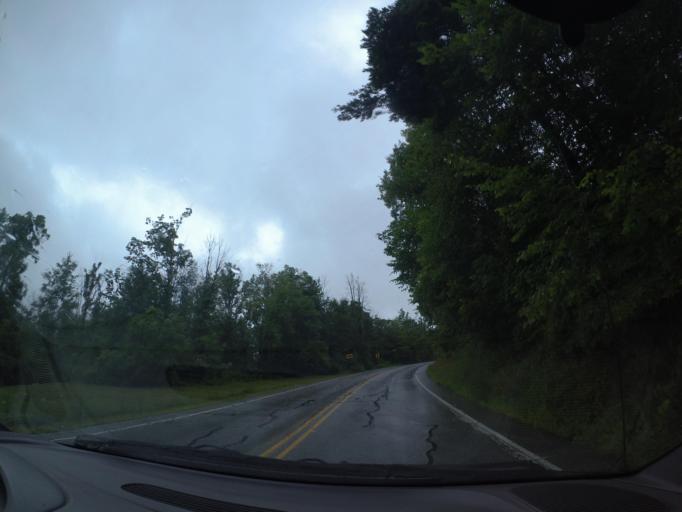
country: US
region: Pennsylvania
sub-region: Erie County
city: Fairview
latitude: 42.0002
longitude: -80.2093
